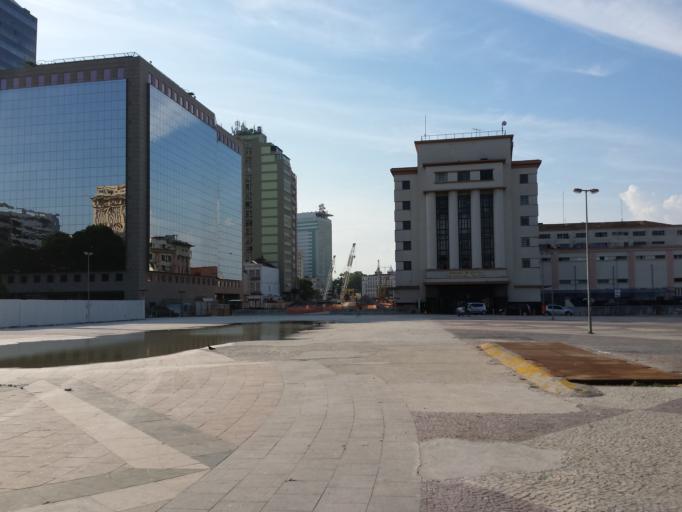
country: BR
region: Rio de Janeiro
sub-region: Rio De Janeiro
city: Rio de Janeiro
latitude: -22.9029
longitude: -43.1730
